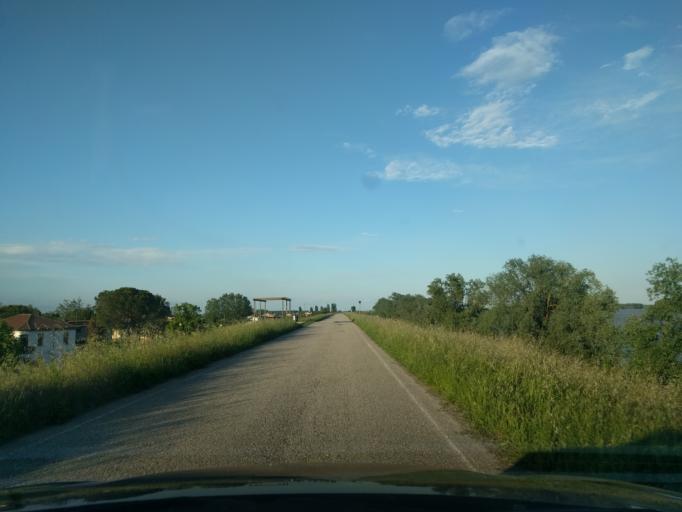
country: IT
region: Veneto
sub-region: Provincia di Rovigo
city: Guarda Veneta
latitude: 44.9787
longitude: 11.8023
